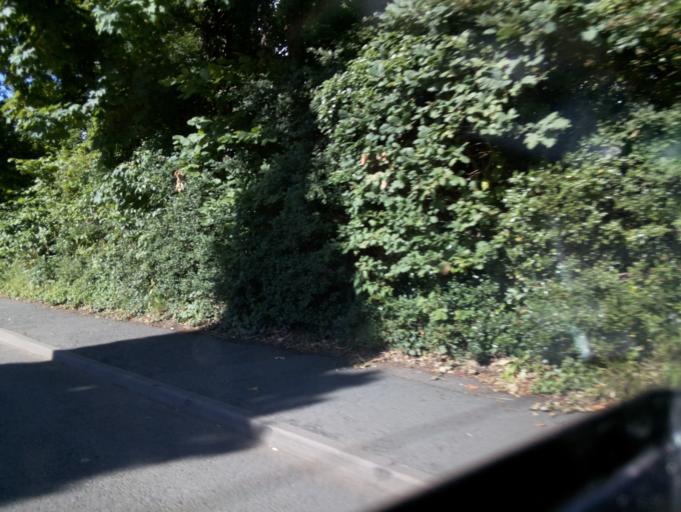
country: GB
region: England
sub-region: Herefordshire
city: Ross on Wye
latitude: 51.9082
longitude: -2.5860
